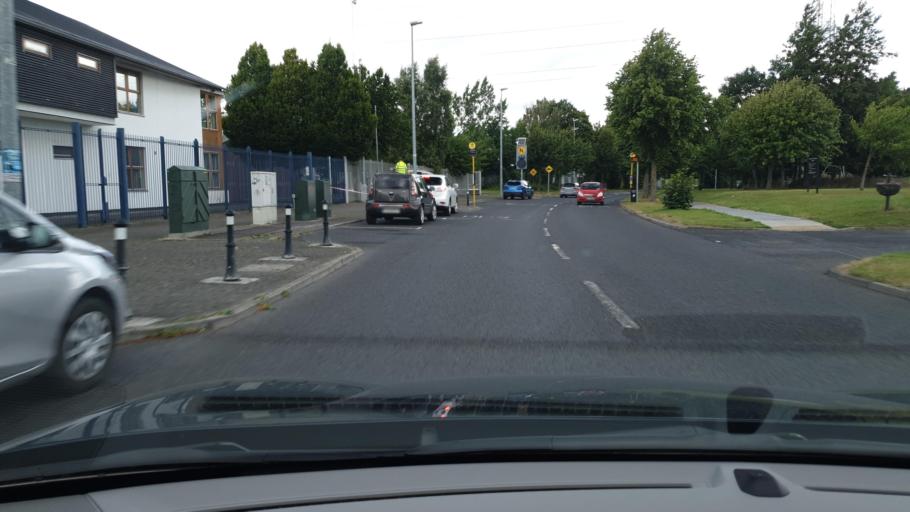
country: IE
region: Leinster
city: Clondalkin
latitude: 53.3245
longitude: -6.4121
